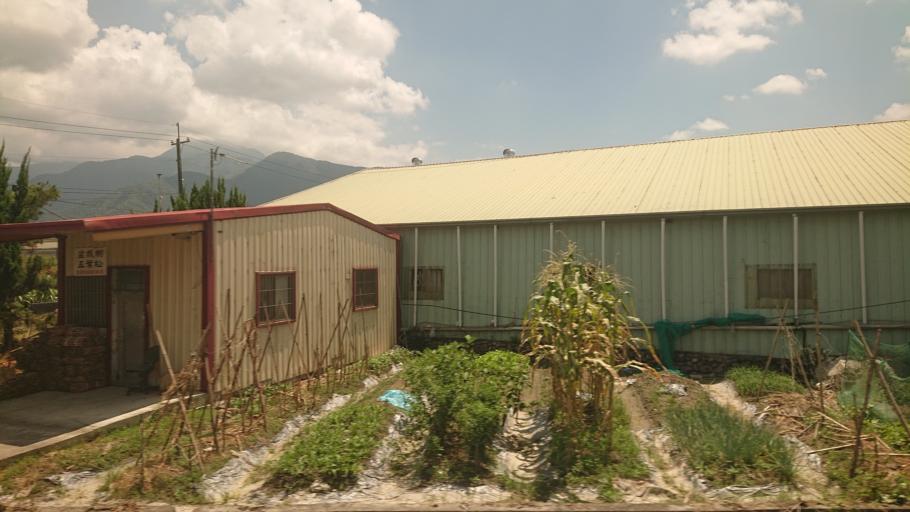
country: TW
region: Taiwan
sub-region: Nantou
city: Puli
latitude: 23.9819
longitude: 120.9601
